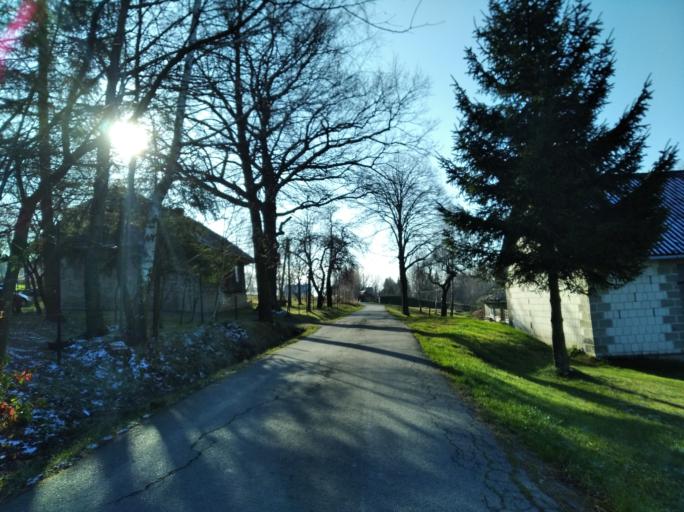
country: PL
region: Subcarpathian Voivodeship
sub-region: Powiat strzyzowski
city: Polomia
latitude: 49.8861
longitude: 21.8498
